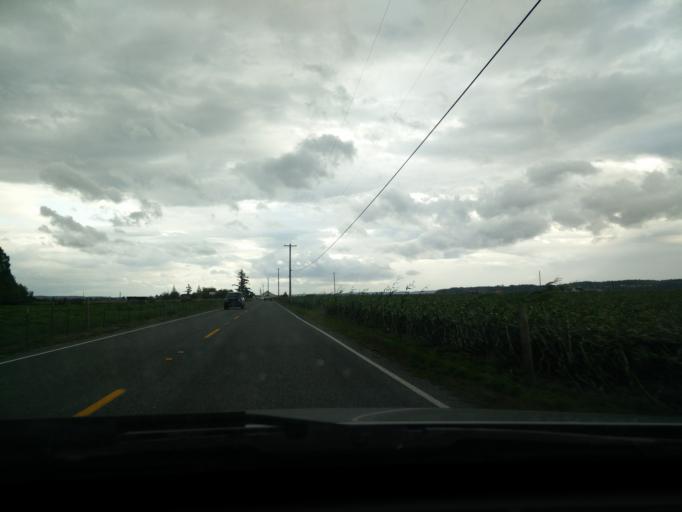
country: US
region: Washington
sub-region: Snohomish County
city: Stanwood
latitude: 48.2673
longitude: -122.3673
